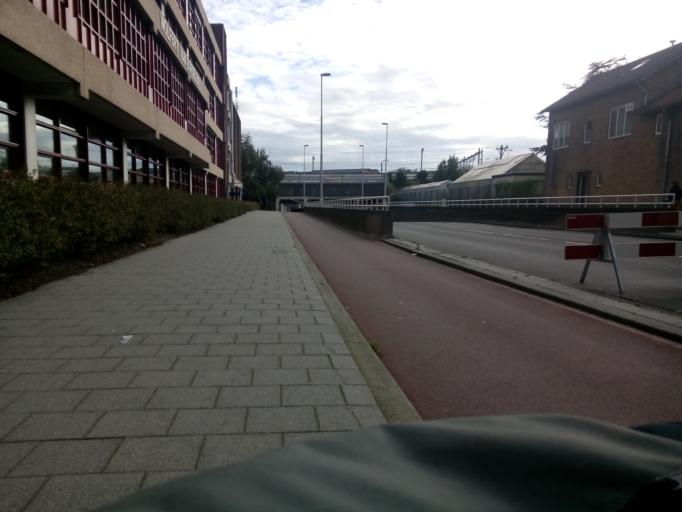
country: NL
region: South Holland
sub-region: Gemeente Rotterdam
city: Delfshaven
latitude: 51.9249
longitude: 4.4546
